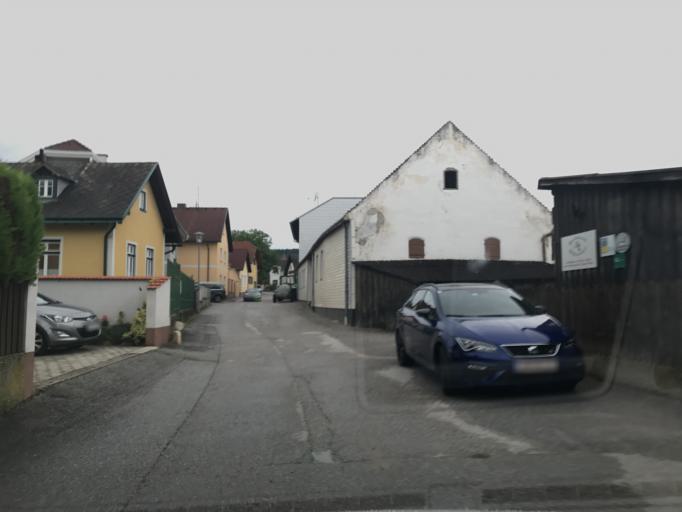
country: AT
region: Lower Austria
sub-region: Politischer Bezirk Wiener Neustadt
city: Markt Piesting
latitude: 47.8560
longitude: 16.1102
